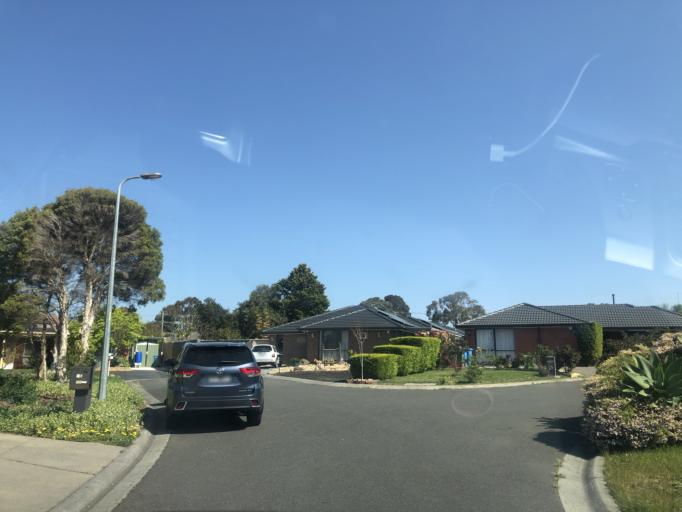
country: AU
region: Victoria
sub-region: Casey
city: Hampton Park
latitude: -38.0397
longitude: 145.2692
